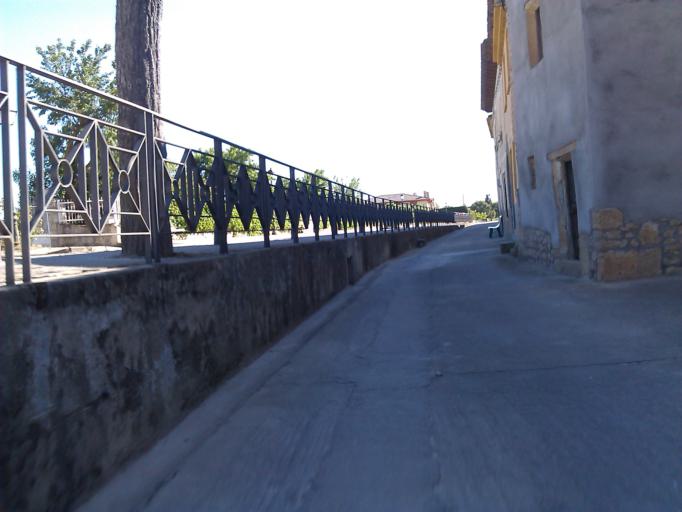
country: ES
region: Castille and Leon
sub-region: Provincia de Burgos
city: Villaquiran de la Puebla
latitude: 42.2892
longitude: -4.1327
